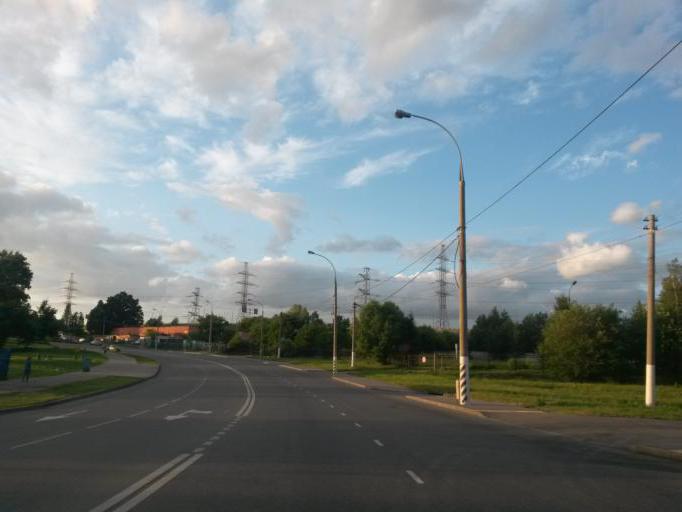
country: RU
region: Moscow
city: Annino
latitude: 55.5700
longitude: 37.5929
